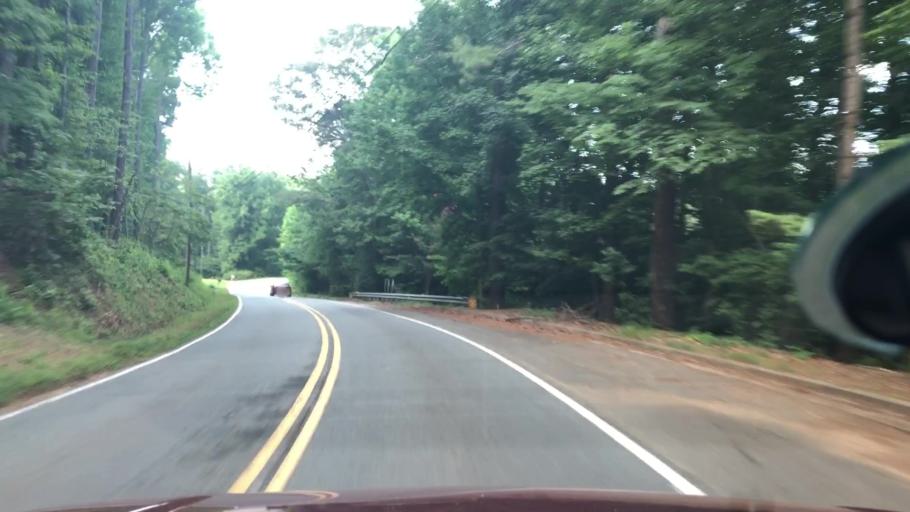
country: US
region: Georgia
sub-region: Cherokee County
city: Woodstock
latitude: 34.1118
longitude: -84.5941
